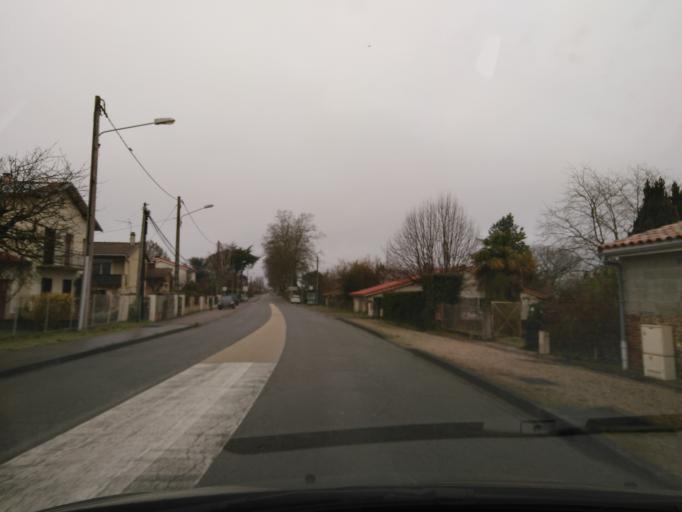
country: FR
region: Midi-Pyrenees
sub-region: Departement de la Haute-Garonne
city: Rieux-Volvestre
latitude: 43.2594
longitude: 1.1932
